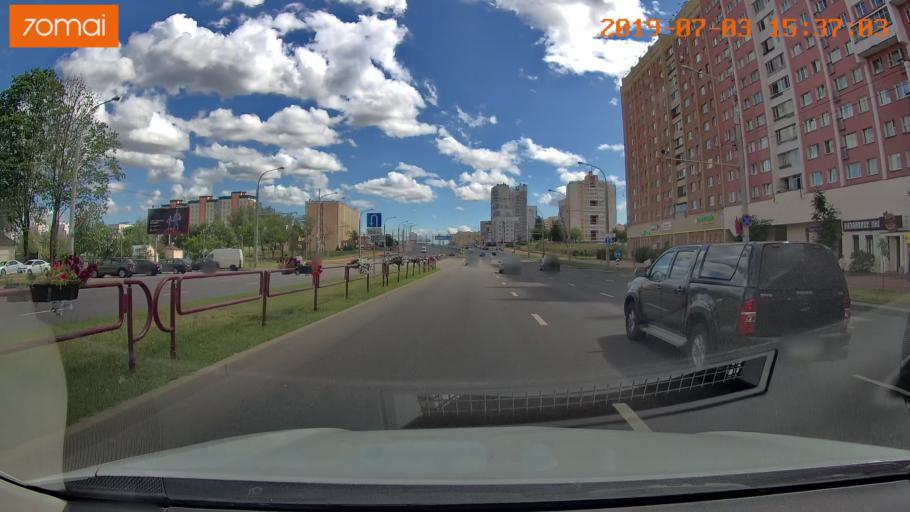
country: BY
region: Minsk
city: Minsk
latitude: 53.8778
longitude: 27.5684
